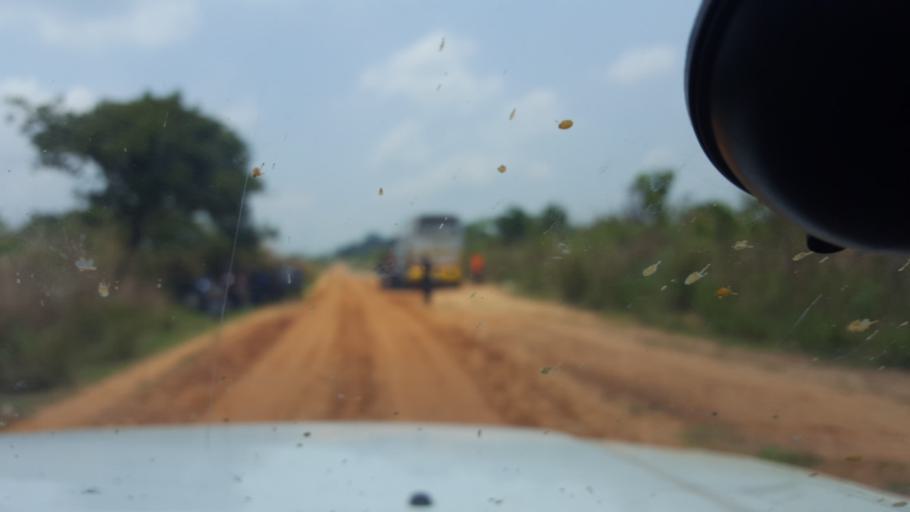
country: CD
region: Bandundu
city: Mushie
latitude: -3.7496
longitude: 16.6622
